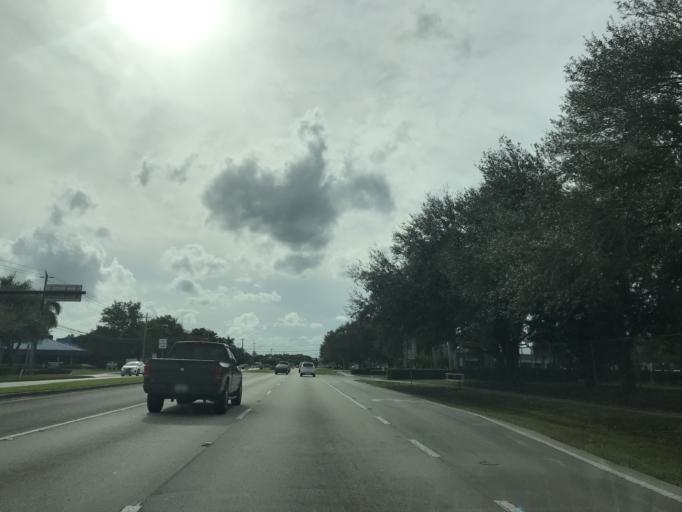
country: US
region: Florida
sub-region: Broward County
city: Coconut Creek
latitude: 26.2575
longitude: -80.1930
